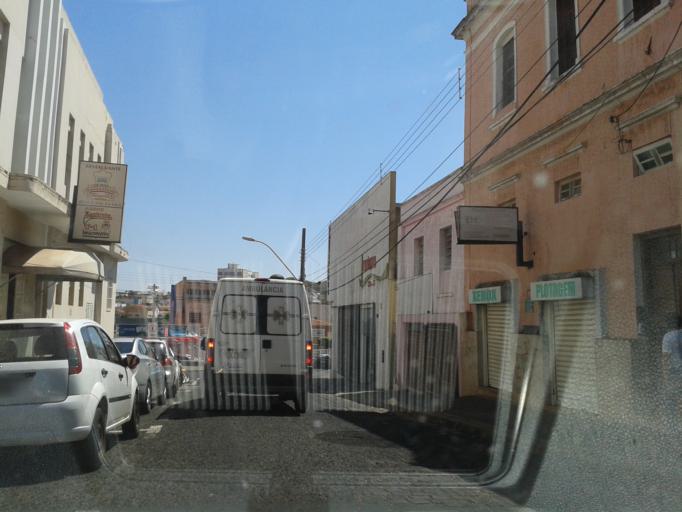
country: BR
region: Minas Gerais
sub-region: Araguari
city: Araguari
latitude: -18.6485
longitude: -48.1903
